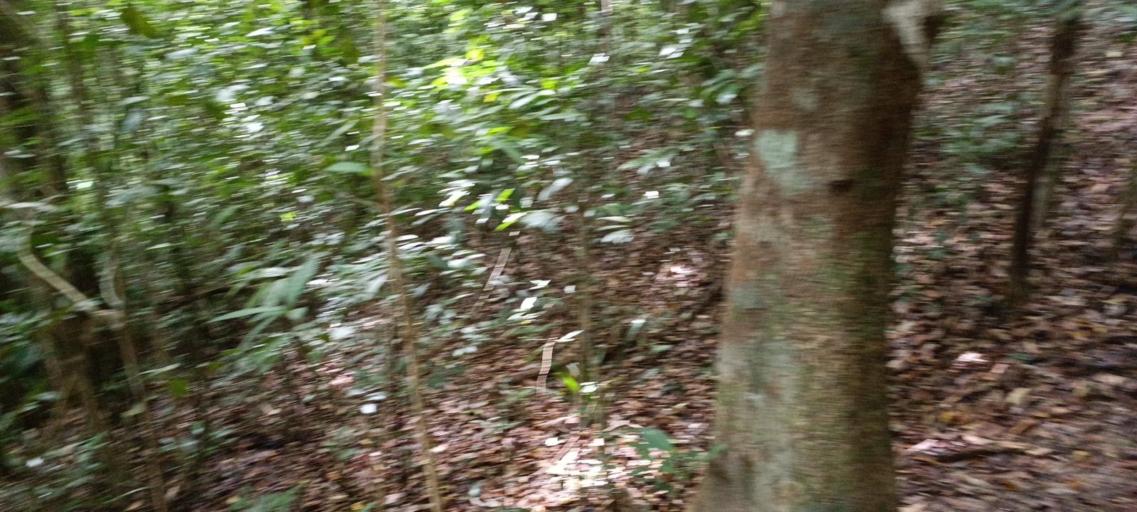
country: MY
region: Penang
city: George Town
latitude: 5.3879
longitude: 100.2930
